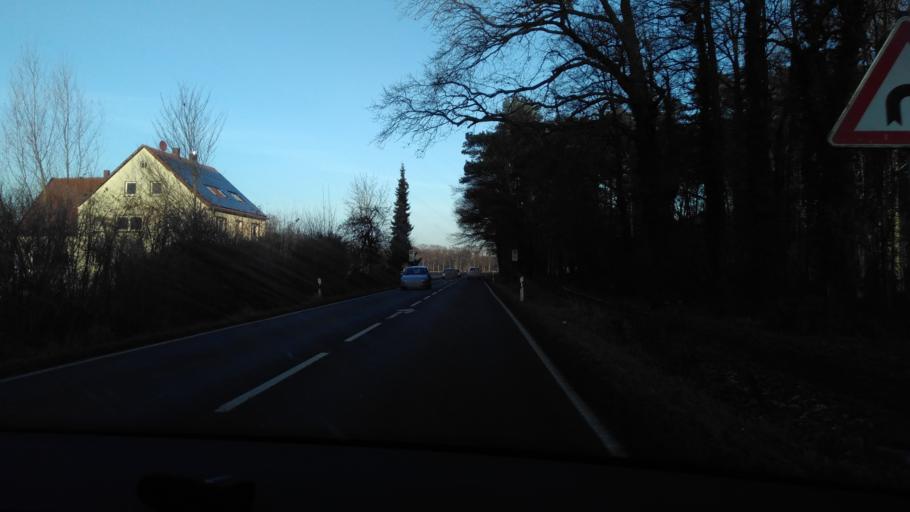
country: DE
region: North Rhine-Westphalia
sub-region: Regierungsbezirk Detmold
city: Verl
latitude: 51.8993
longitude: 8.5364
